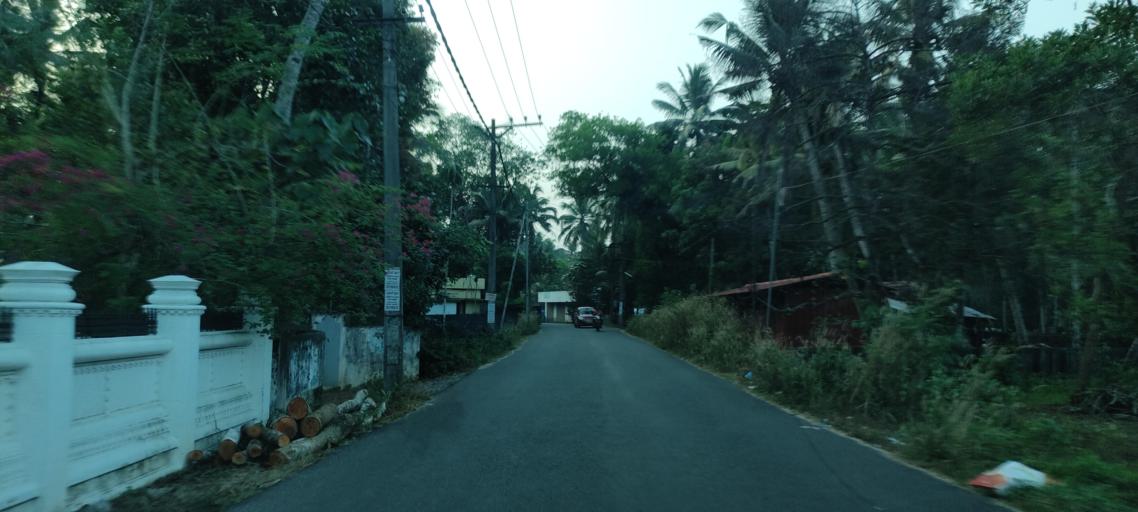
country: IN
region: Kerala
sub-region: Alappuzha
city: Kayankulam
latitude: 9.1373
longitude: 76.5186
